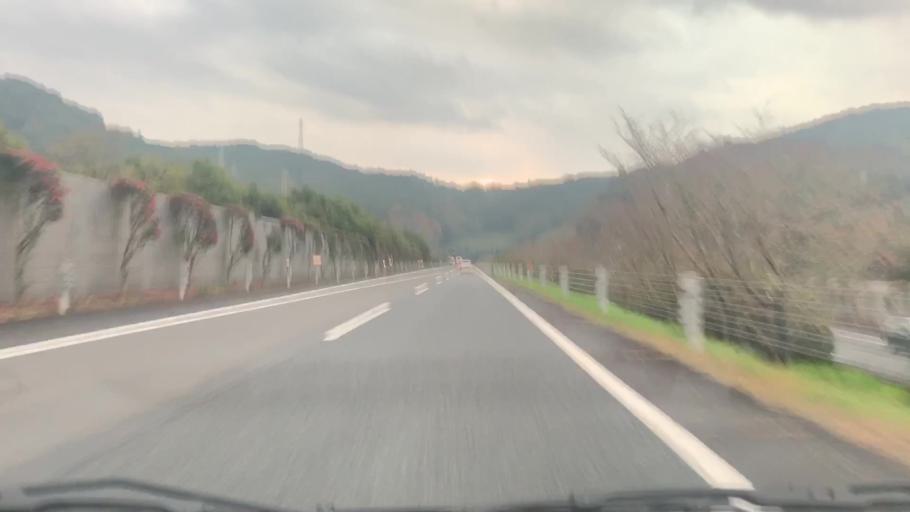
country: JP
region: Nagasaki
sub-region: Isahaya-shi
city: Isahaya
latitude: 32.8788
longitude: 129.9966
